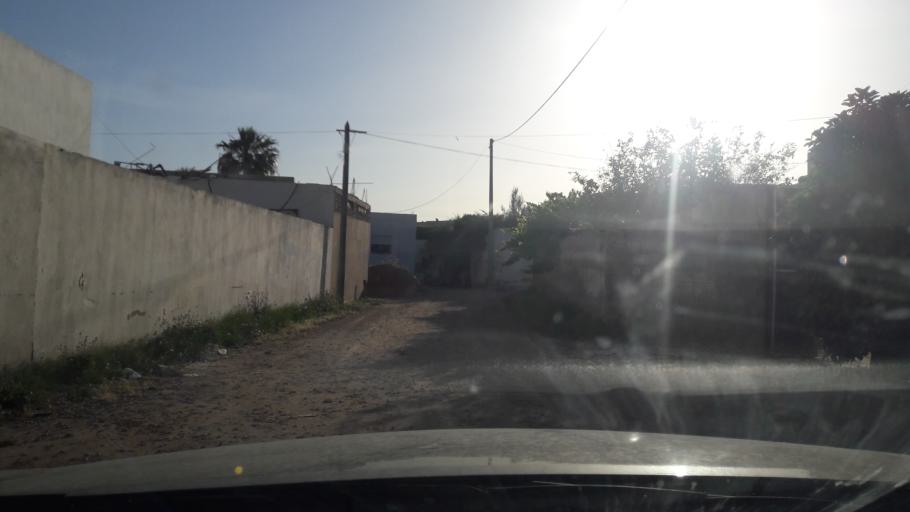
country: TN
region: Safaqis
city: Al Qarmadah
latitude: 34.7964
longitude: 10.7601
